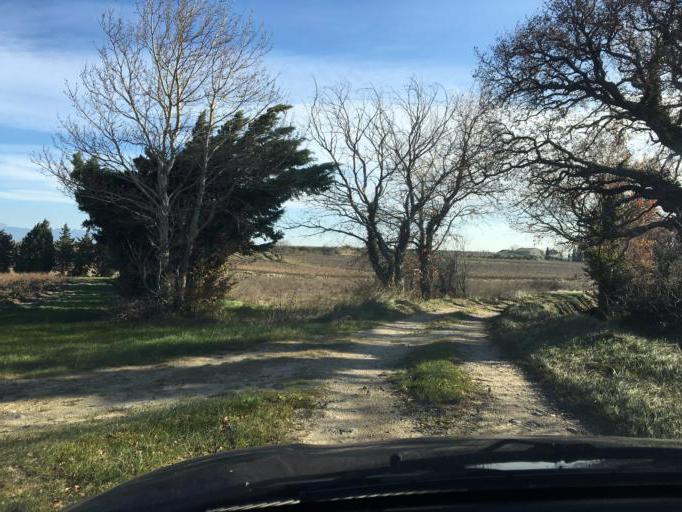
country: FR
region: Provence-Alpes-Cote d'Azur
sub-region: Departement du Vaucluse
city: Camaret-sur-Aigues
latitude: 44.1458
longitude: 4.8968
